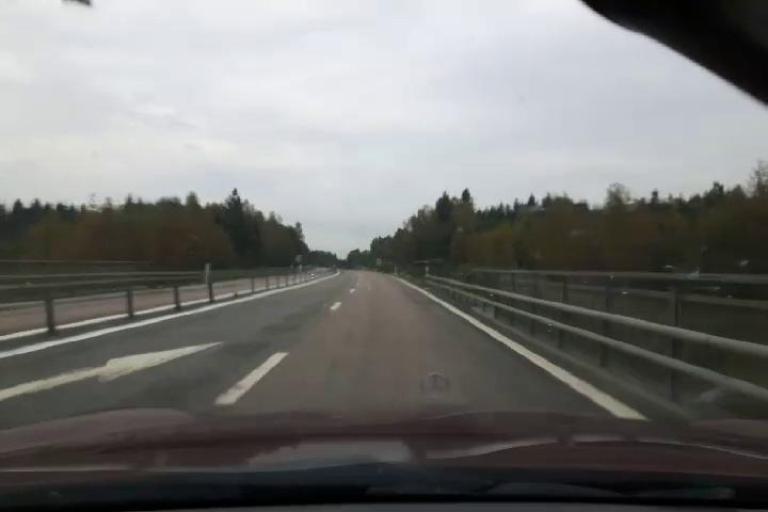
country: SE
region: Vaesternorrland
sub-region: Haernoesands Kommun
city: Haernoesand
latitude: 62.8650
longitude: 18.0356
